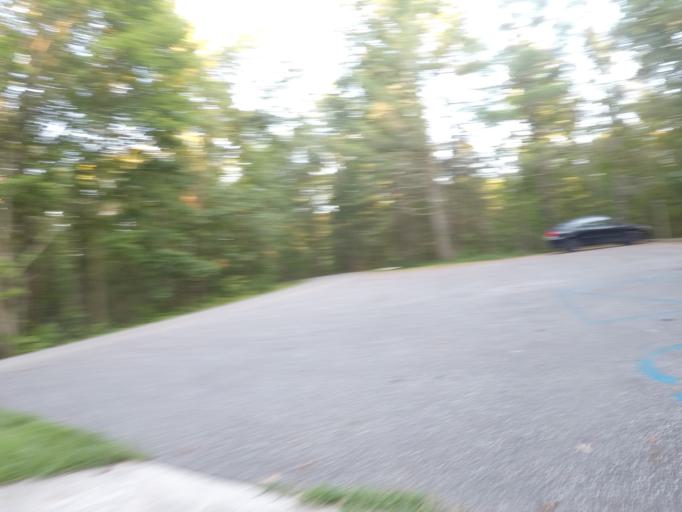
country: US
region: Ohio
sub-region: Lawrence County
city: Ironton
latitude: 38.6119
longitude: -82.6196
